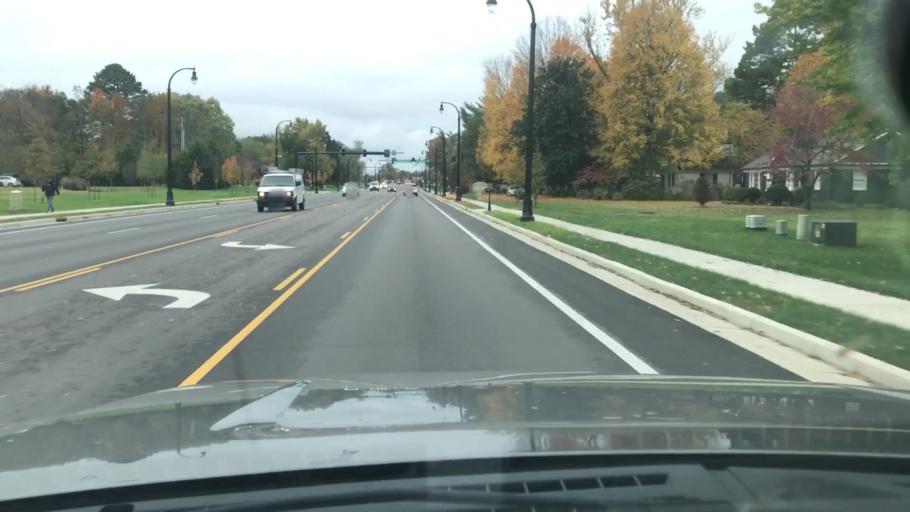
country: US
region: Tennessee
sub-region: Williamson County
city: Franklin
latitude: 35.9387
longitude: -86.8793
